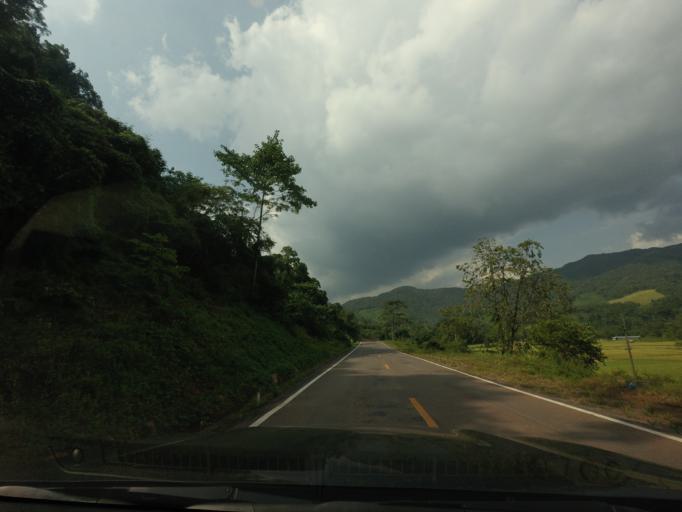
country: TH
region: Nan
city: Bo Kluea
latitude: 19.2264
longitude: 101.1824
